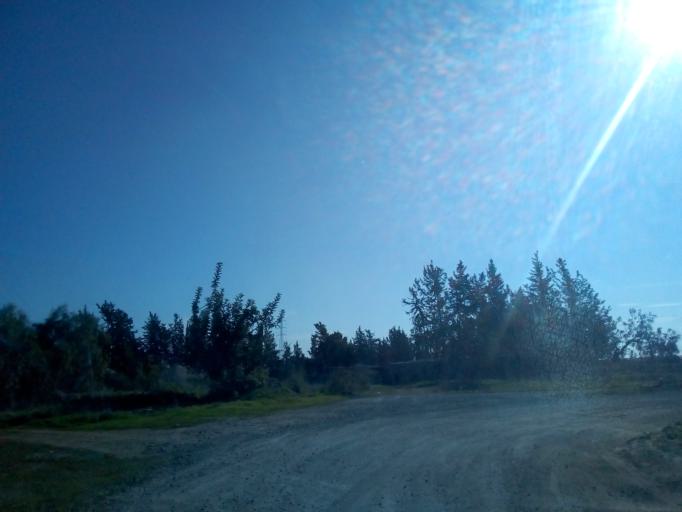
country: CY
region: Limassol
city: Ypsonas
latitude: 34.6779
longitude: 32.9792
